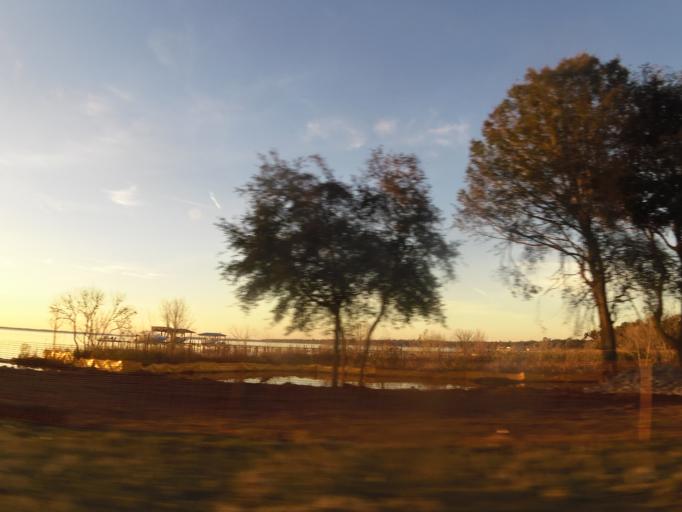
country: US
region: Florida
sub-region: Clay County
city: Green Cove Springs
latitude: 29.9908
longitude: -81.6086
